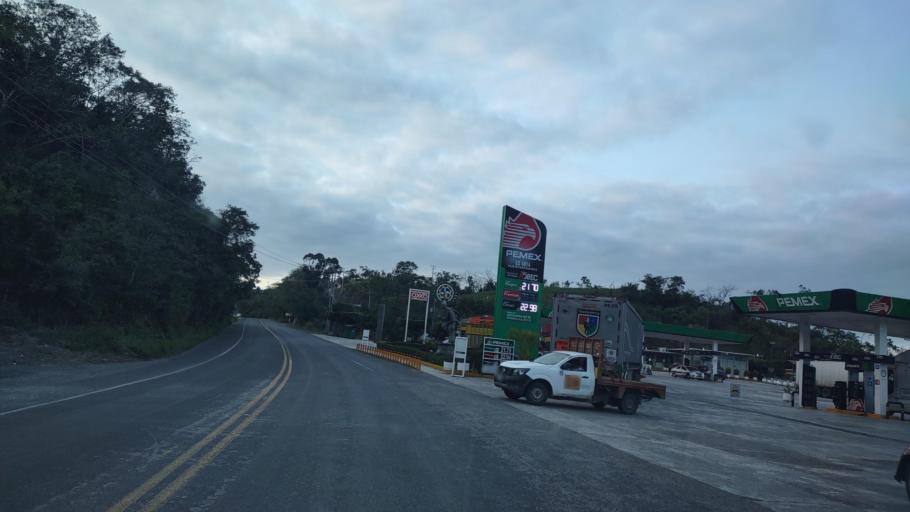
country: MX
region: Veracruz
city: Papantla de Olarte
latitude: 20.4630
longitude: -97.3066
